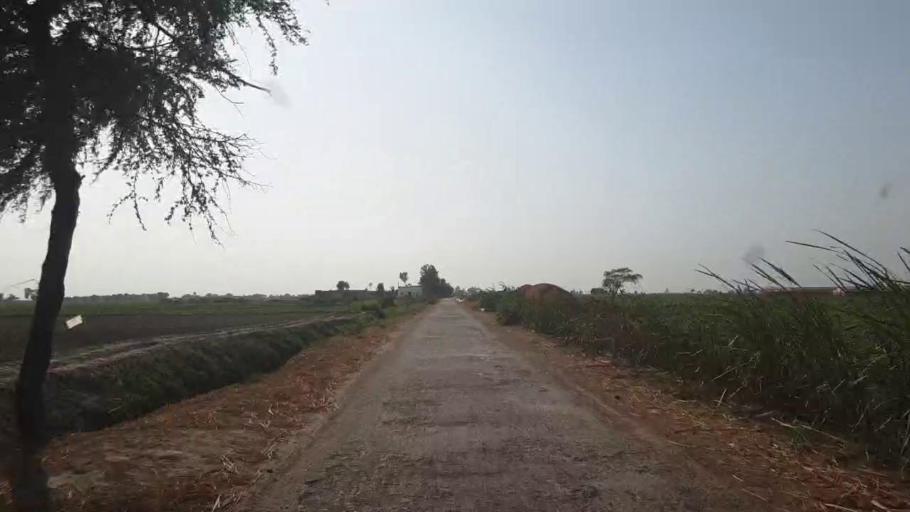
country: PK
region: Sindh
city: Kario
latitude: 24.5764
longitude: 68.5072
